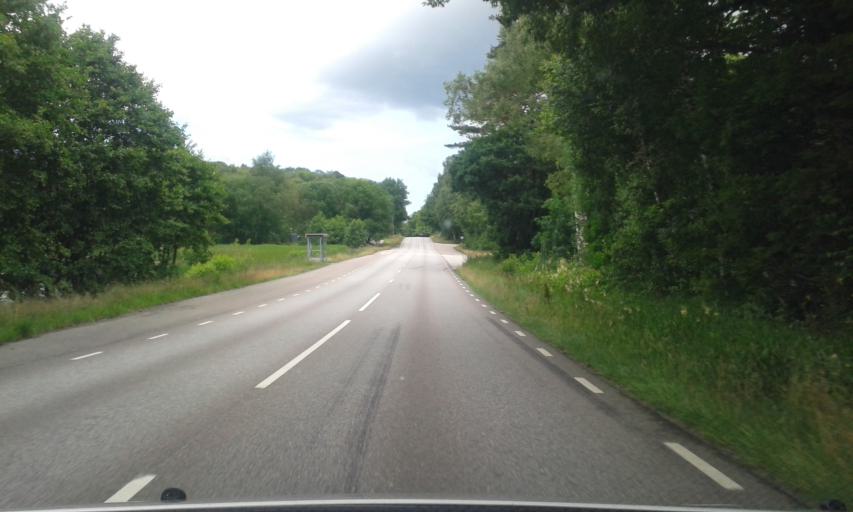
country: SE
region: Vaestra Goetaland
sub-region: Kungalvs Kommun
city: Kode
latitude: 57.9314
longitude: 11.8916
